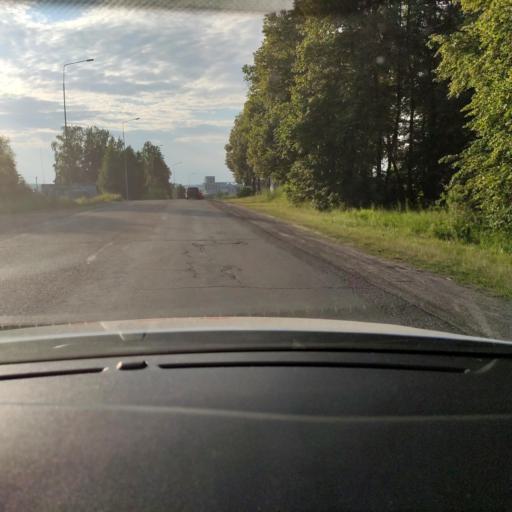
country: RU
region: Tatarstan
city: Vysokaya Gora
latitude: 55.9743
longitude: 49.3115
